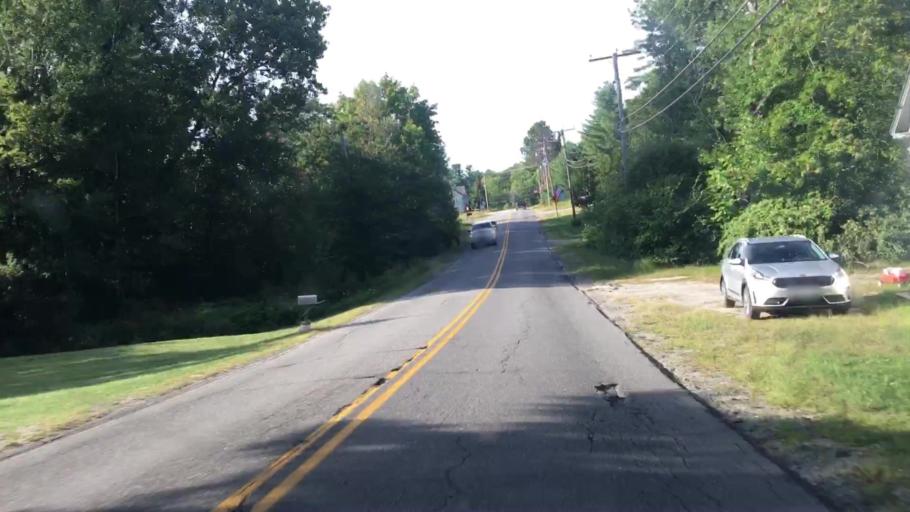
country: US
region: Maine
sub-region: Penobscot County
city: Enfield
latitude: 45.2446
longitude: -68.5652
